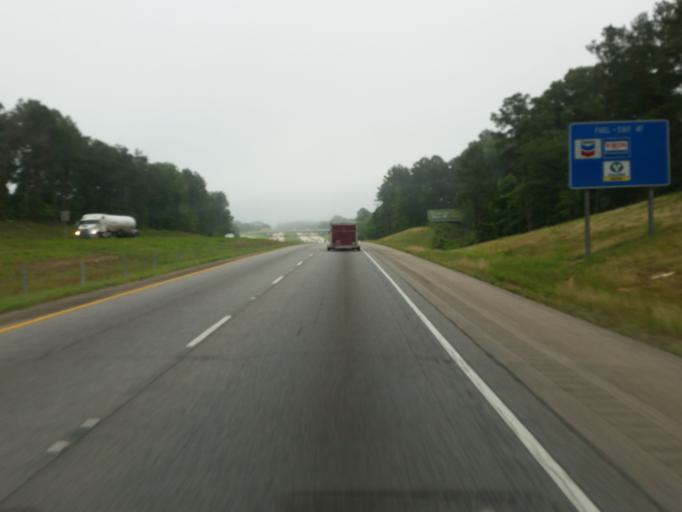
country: US
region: Louisiana
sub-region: Webster Parish
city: Minden
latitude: 32.5917
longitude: -93.3027
